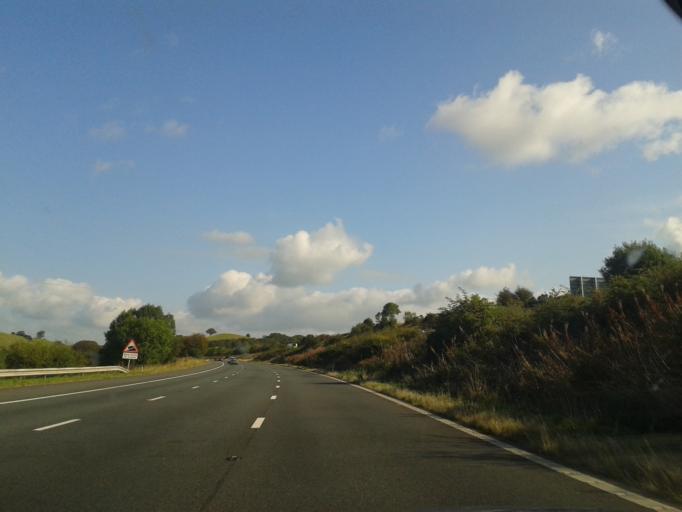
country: GB
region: England
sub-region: Cumbria
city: Milnthorpe
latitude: 54.2432
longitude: -2.7028
